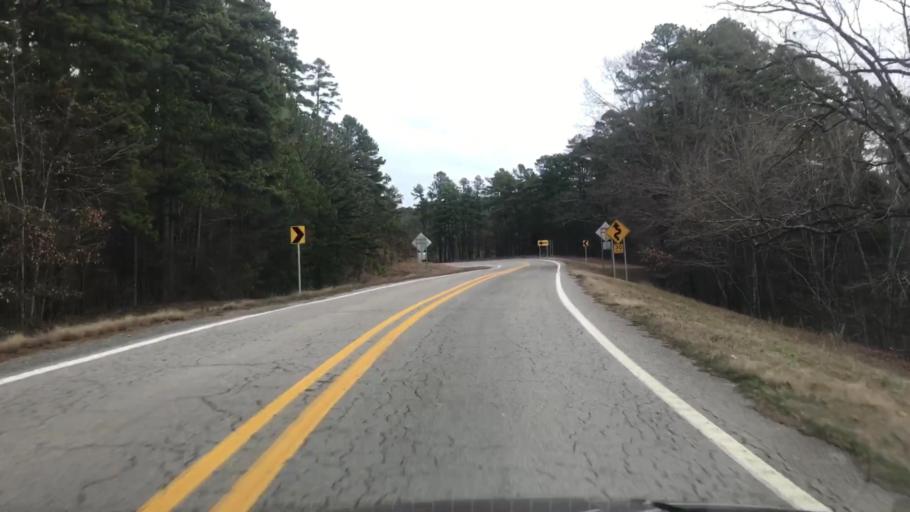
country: US
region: Arkansas
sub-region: Montgomery County
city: Mount Ida
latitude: 34.6741
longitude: -93.7855
